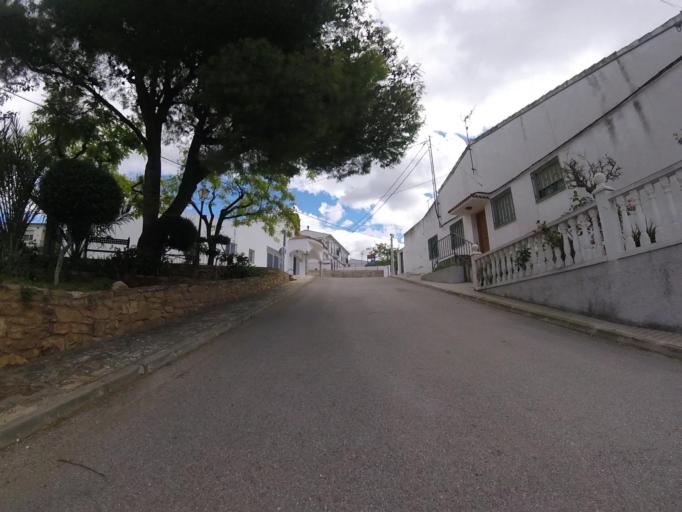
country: ES
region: Valencia
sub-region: Provincia de Castello
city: Sierra-Engarceran
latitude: 40.2926
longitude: -0.0465
